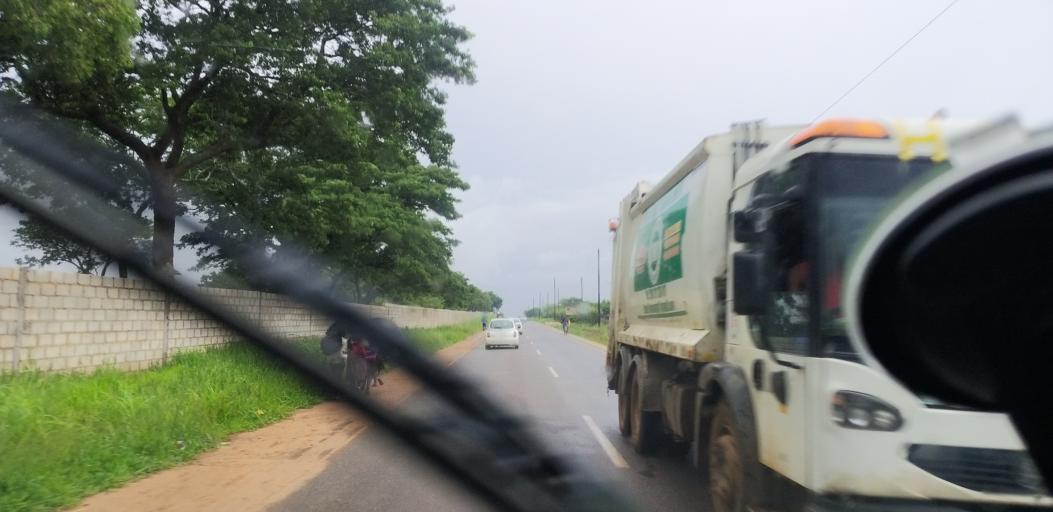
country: ZM
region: Lusaka
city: Lusaka
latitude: -15.5130
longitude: 28.3113
